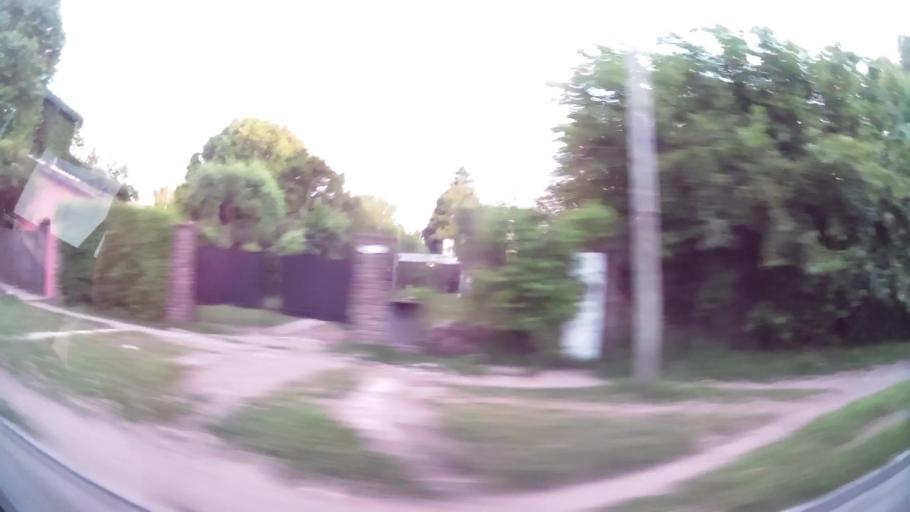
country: AR
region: Buenos Aires
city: Santa Catalina - Dique Lujan
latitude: -34.4742
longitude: -58.7655
